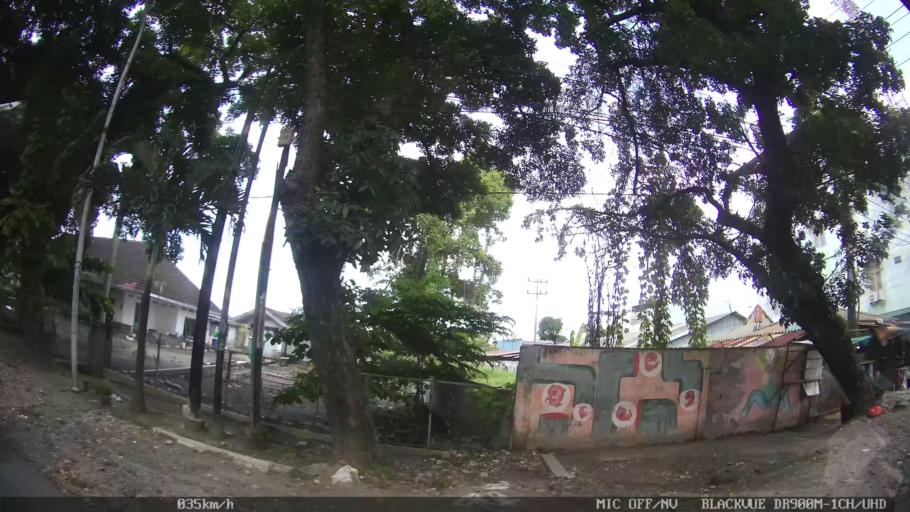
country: ID
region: North Sumatra
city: Medan
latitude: 3.6174
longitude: 98.6718
